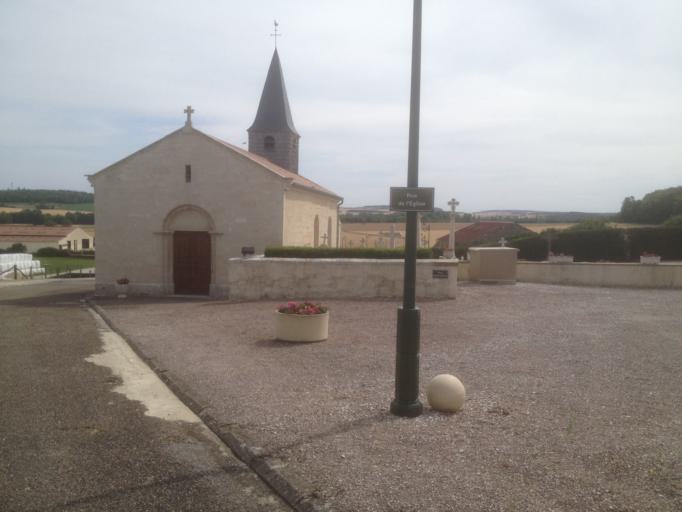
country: FR
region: Champagne-Ardenne
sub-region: Departement de la Haute-Marne
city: Joinville
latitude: 48.4558
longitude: 5.2862
